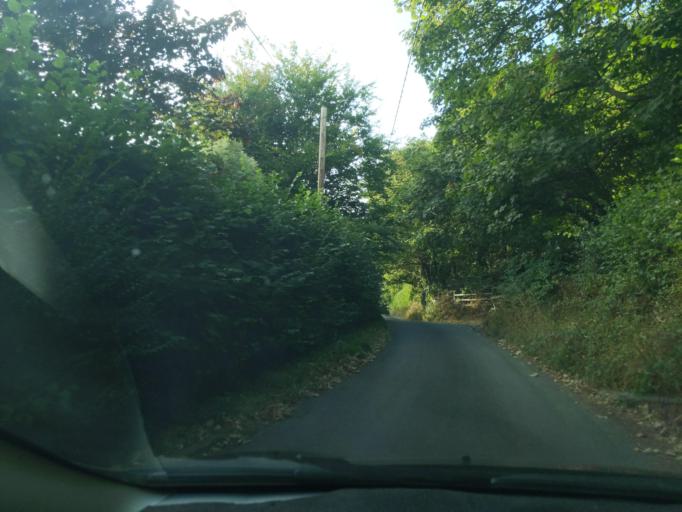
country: GB
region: England
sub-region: Devon
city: Salcombe
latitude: 50.2283
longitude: -3.7927
